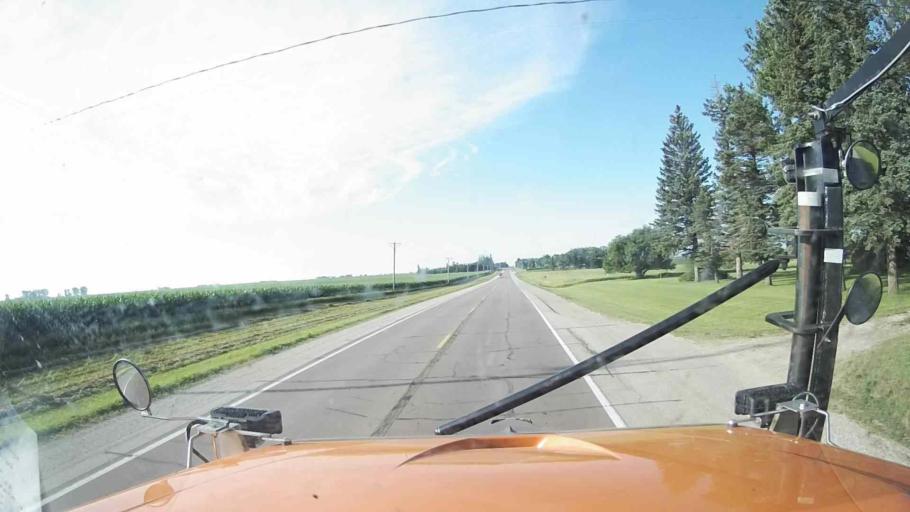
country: US
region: Iowa
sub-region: Cerro Gordo County
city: Mason City
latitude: 43.0776
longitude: -93.2015
